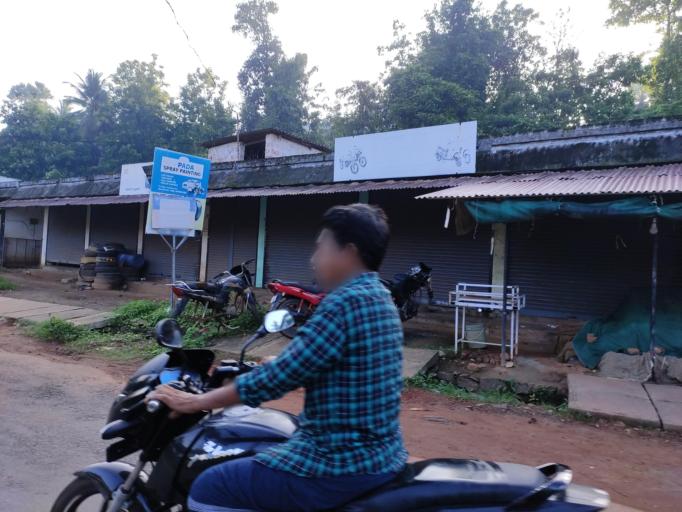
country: IN
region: Kerala
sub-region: Palakkad district
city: Mannarakkat
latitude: 10.9789
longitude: 76.4631
